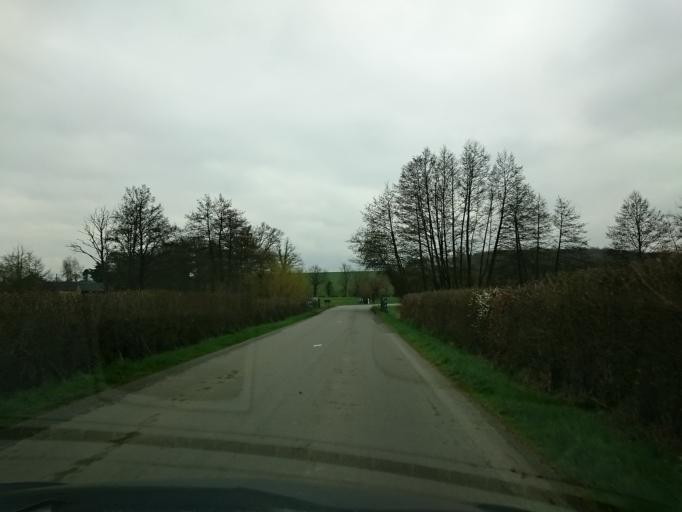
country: FR
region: Brittany
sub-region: Departement d'Ille-et-Vilaine
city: Corps-Nuds
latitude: 47.9727
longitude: -1.5909
